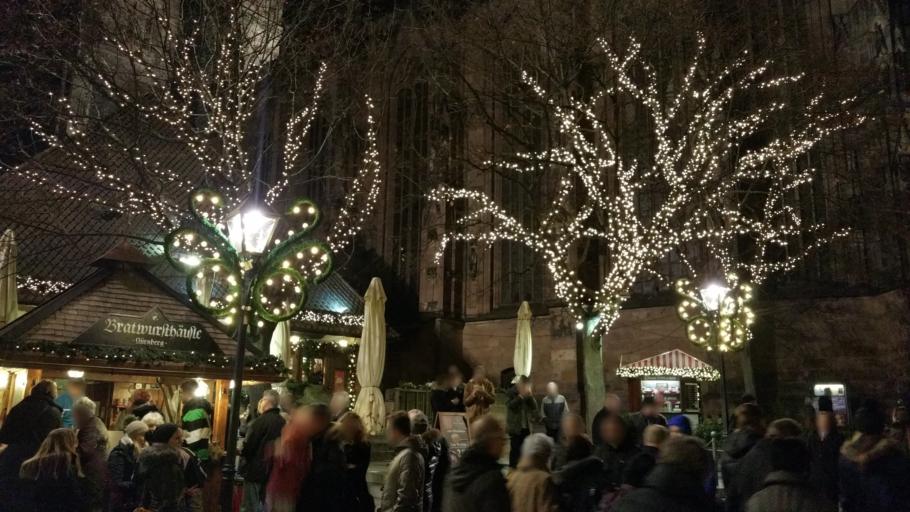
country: DE
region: Bavaria
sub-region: Regierungsbezirk Mittelfranken
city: Nuernberg
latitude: 49.4547
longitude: 11.0769
